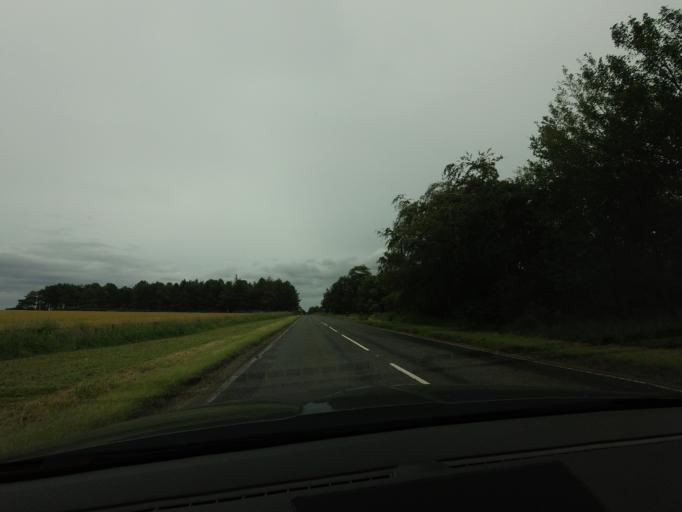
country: GB
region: Scotland
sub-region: Moray
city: Buckie
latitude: 57.6678
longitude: -2.9324
